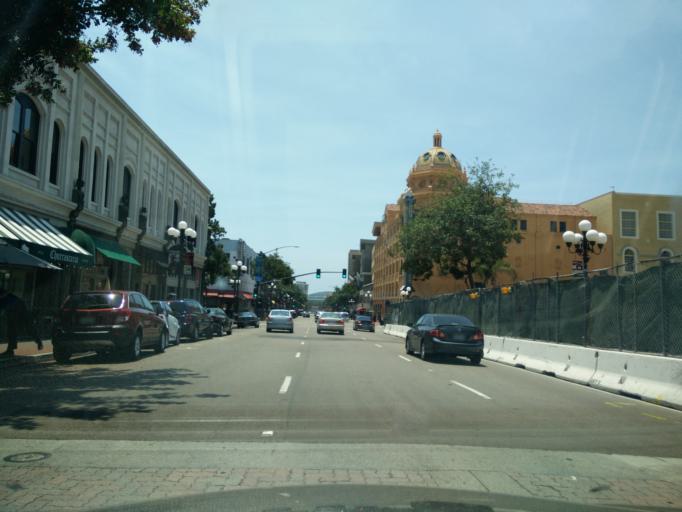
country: US
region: California
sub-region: San Diego County
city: San Diego
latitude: 32.7153
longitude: -117.1611
